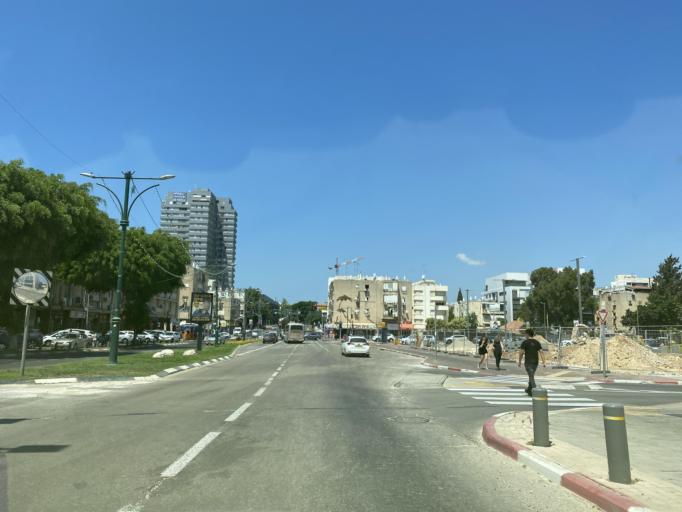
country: IL
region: Tel Aviv
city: Herzliyya
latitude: 32.1638
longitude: 34.8426
